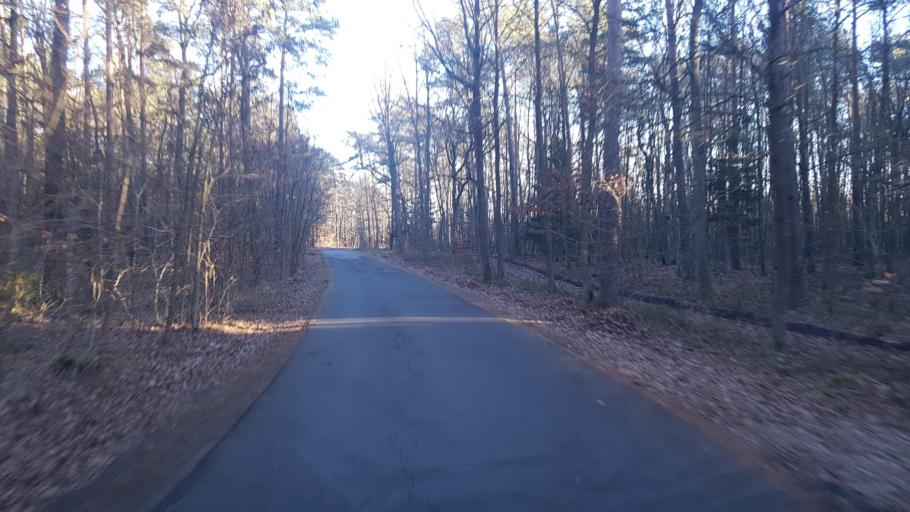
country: DE
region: Brandenburg
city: Tauer
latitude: 51.9362
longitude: 14.4581
